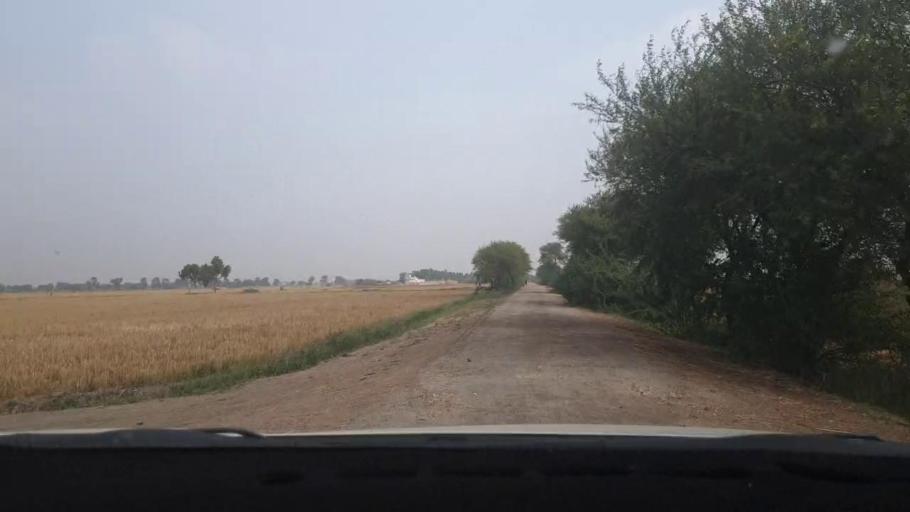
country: PK
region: Sindh
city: Tando Muhammad Khan
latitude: 25.0564
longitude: 68.5332
